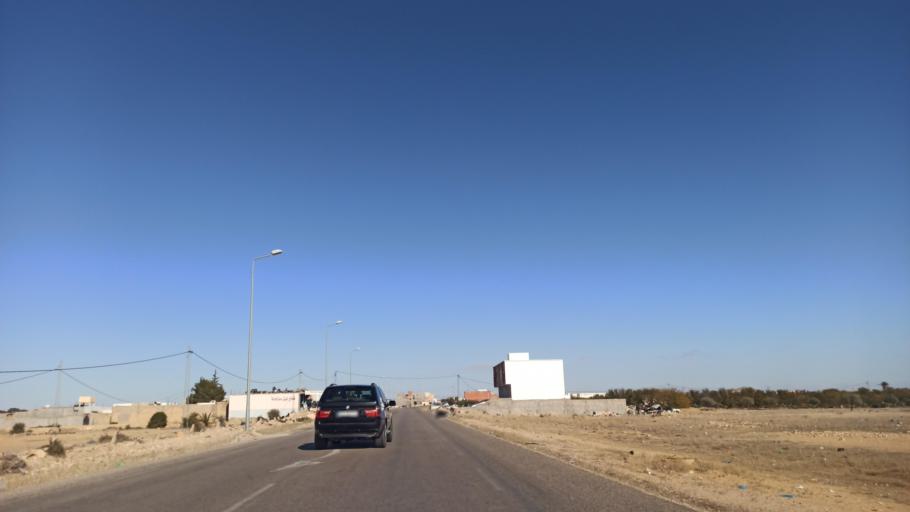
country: TN
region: Sidi Bu Zayd
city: Jilma
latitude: 35.2609
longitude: 9.4059
